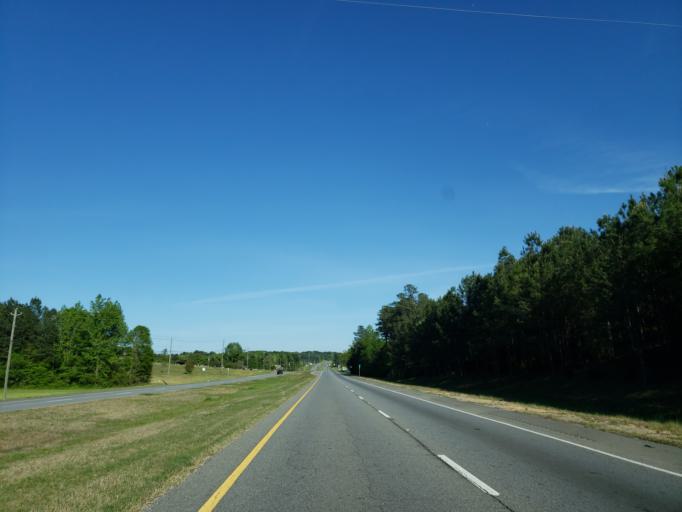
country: US
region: Georgia
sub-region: Polk County
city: Cedartown
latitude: 34.0171
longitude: -85.2040
